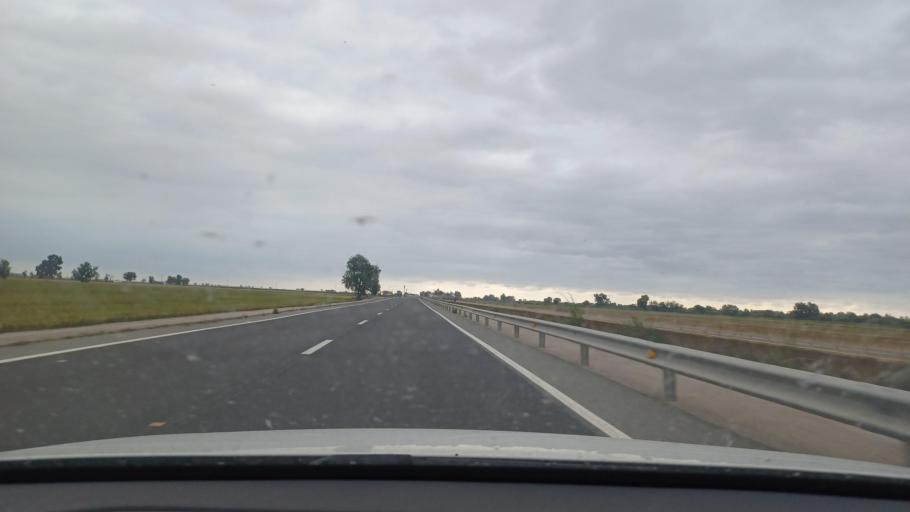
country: ES
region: Catalonia
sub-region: Provincia de Tarragona
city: Amposta
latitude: 40.7150
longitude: 0.6275
